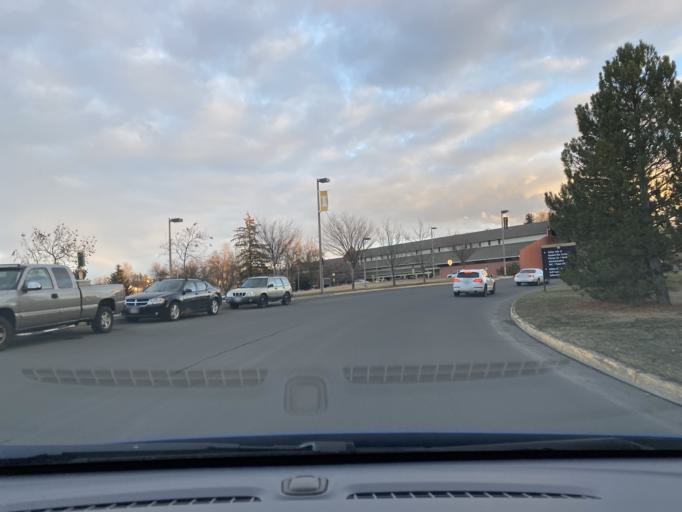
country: US
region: Idaho
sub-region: Latah County
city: Moscow
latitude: 46.7305
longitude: -117.0219
